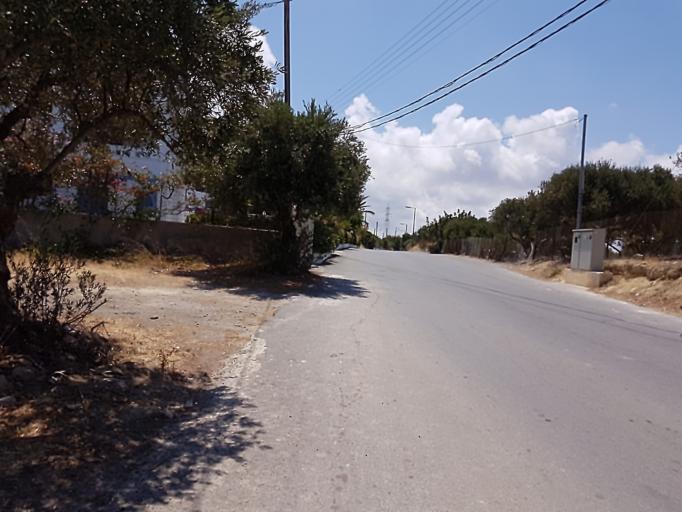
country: GR
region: Crete
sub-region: Nomos Irakleiou
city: Limin Khersonisou
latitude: 35.3166
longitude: 25.3827
